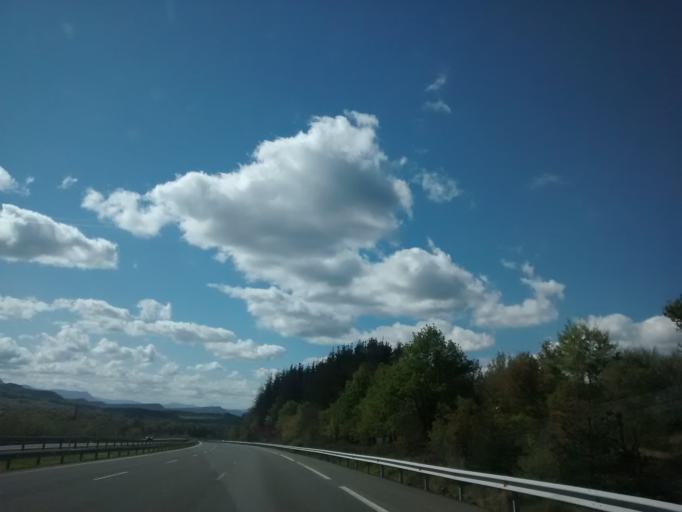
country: ES
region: Basque Country
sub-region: Provincia de Alava
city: Murguia
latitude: 43.0003
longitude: -2.8883
